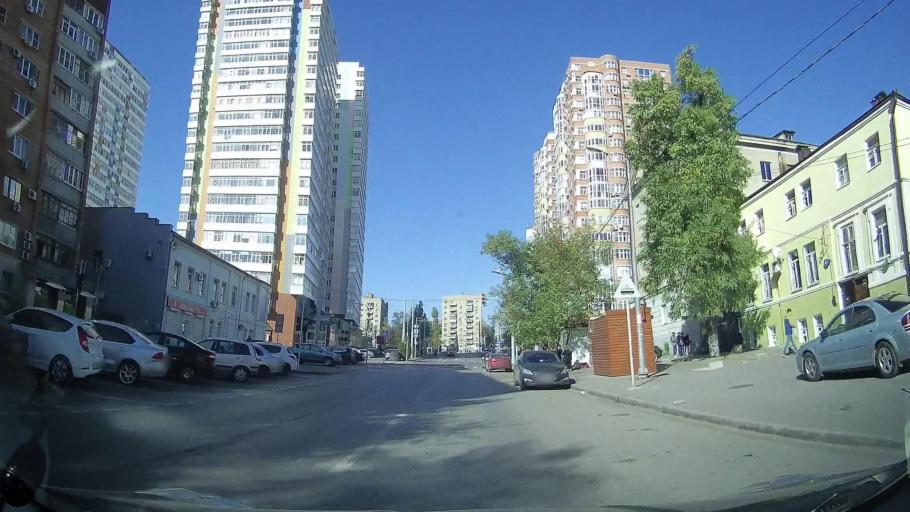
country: RU
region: Rostov
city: Rostov-na-Donu
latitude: 47.2223
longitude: 39.6970
